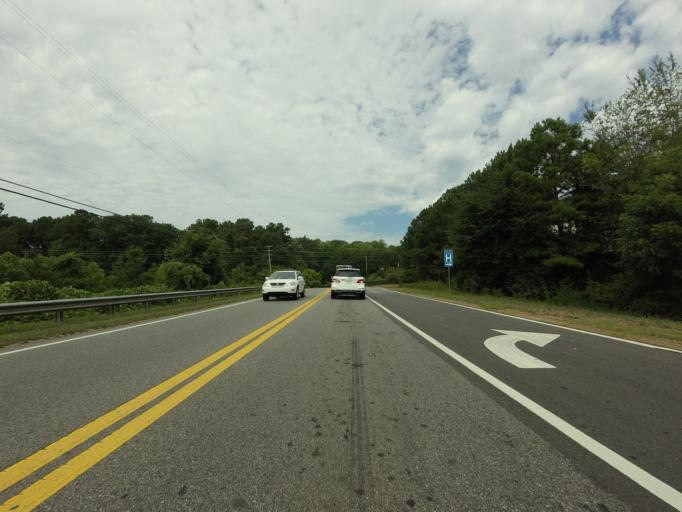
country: US
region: Georgia
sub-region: Fulton County
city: Johns Creek
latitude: 34.0332
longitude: -84.1689
